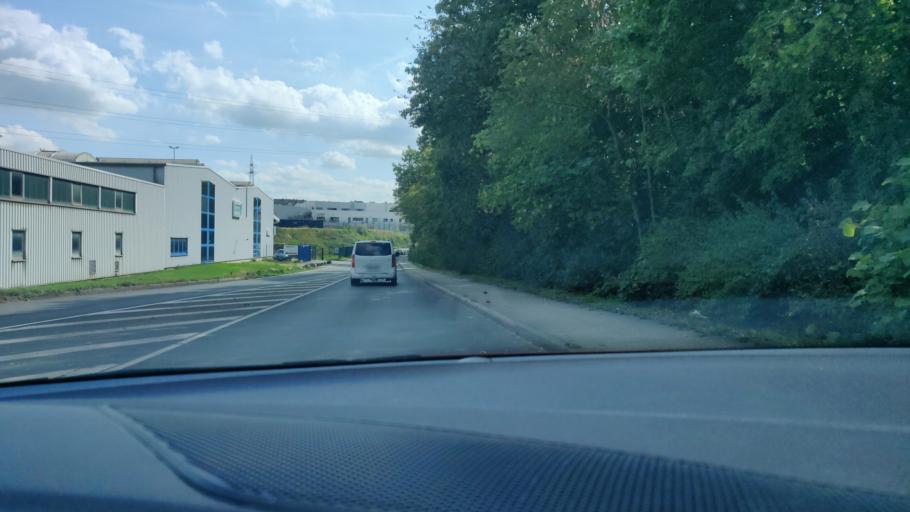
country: DE
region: North Rhine-Westphalia
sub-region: Regierungsbezirk Dusseldorf
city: Velbert
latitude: 51.3446
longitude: 7.0576
